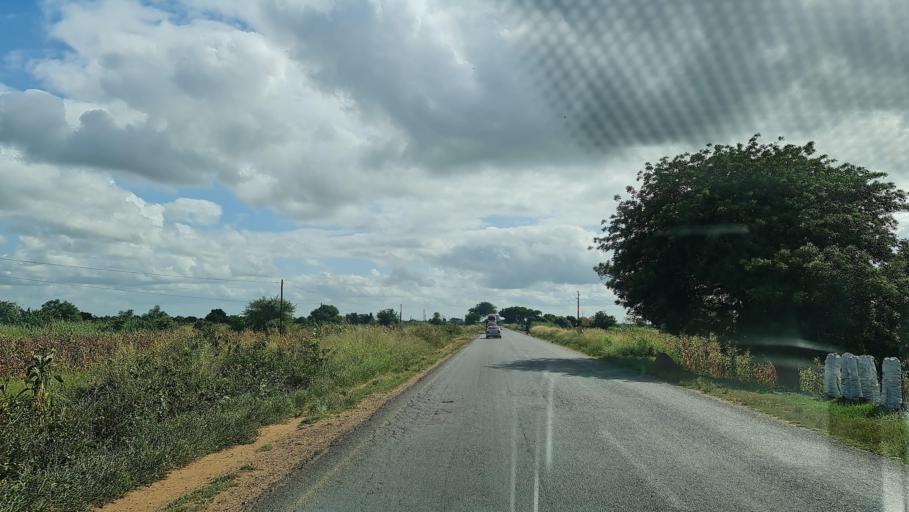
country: MZ
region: Gaza
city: Macia
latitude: -25.0837
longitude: 32.8469
